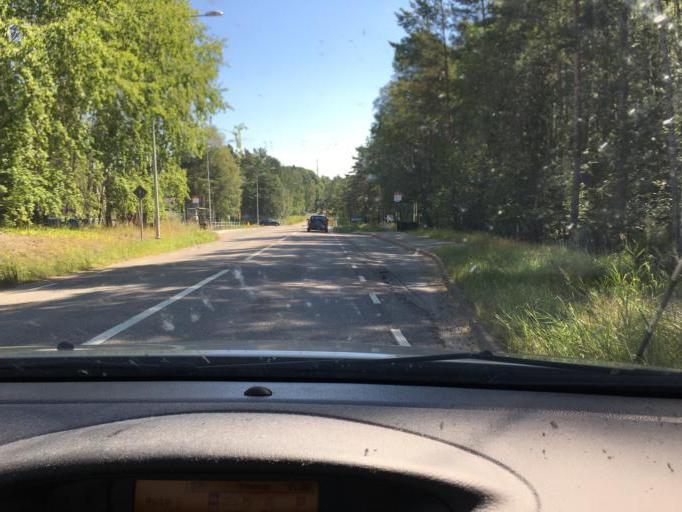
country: SE
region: Stockholm
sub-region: Varmdo Kommun
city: Mortnas
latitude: 59.2776
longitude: 18.4466
